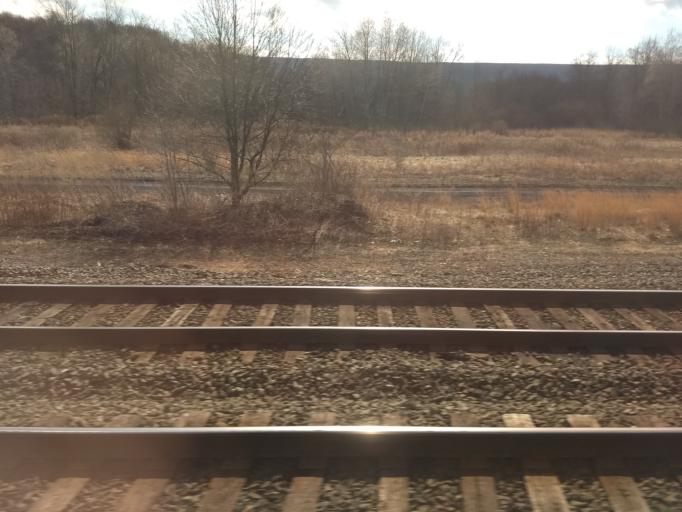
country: US
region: Pennsylvania
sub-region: Blair County
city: Greenwood
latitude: 40.5719
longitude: -78.3558
